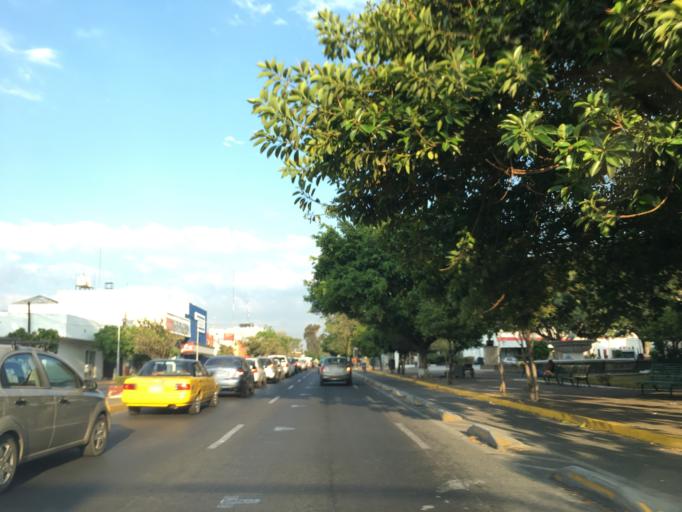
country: MX
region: Jalisco
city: Guadalajara
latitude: 20.6703
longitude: -103.3569
